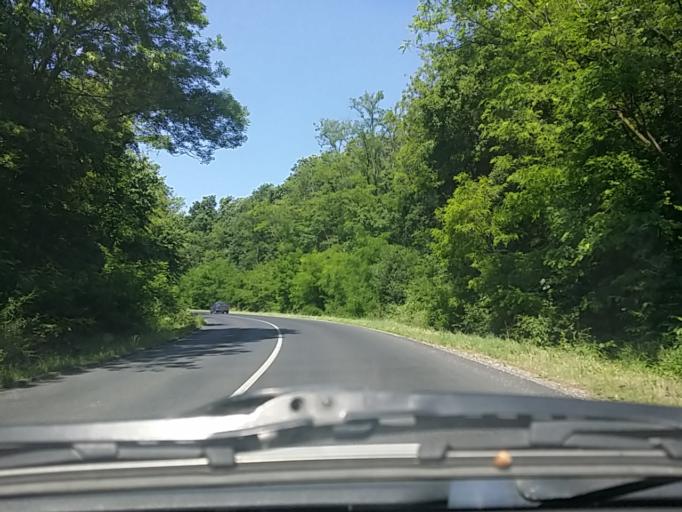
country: HU
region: Pest
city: Csobanka
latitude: 47.6677
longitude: 18.9635
